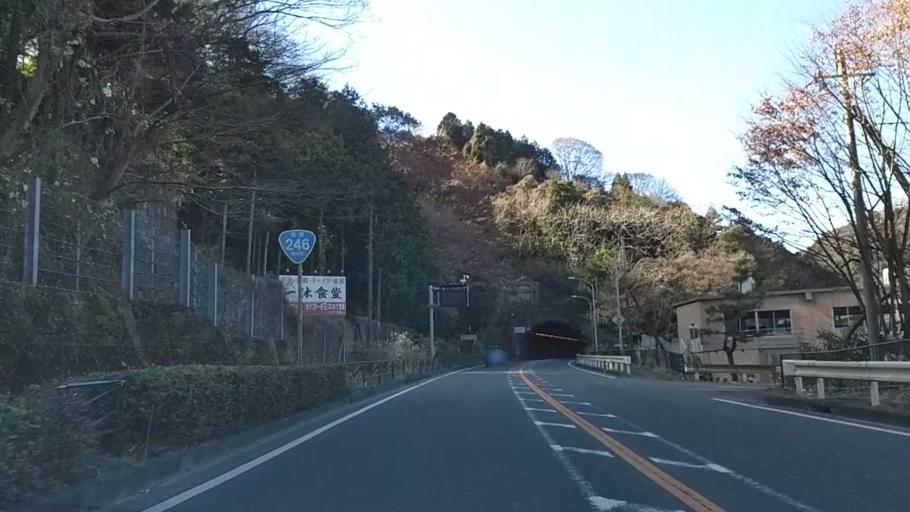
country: JP
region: Kanagawa
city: Odawara
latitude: 35.3588
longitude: 139.0760
